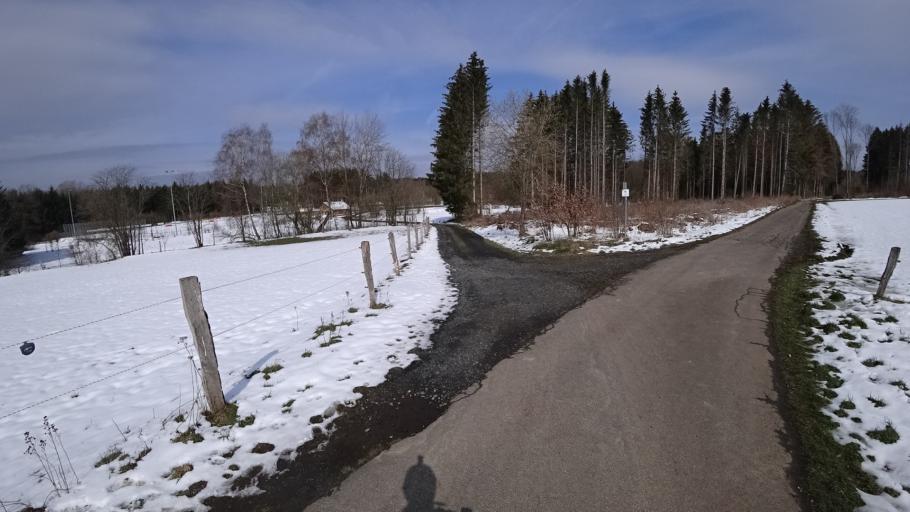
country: DE
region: Rheinland-Pfalz
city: Morlen
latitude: 50.7041
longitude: 7.8845
